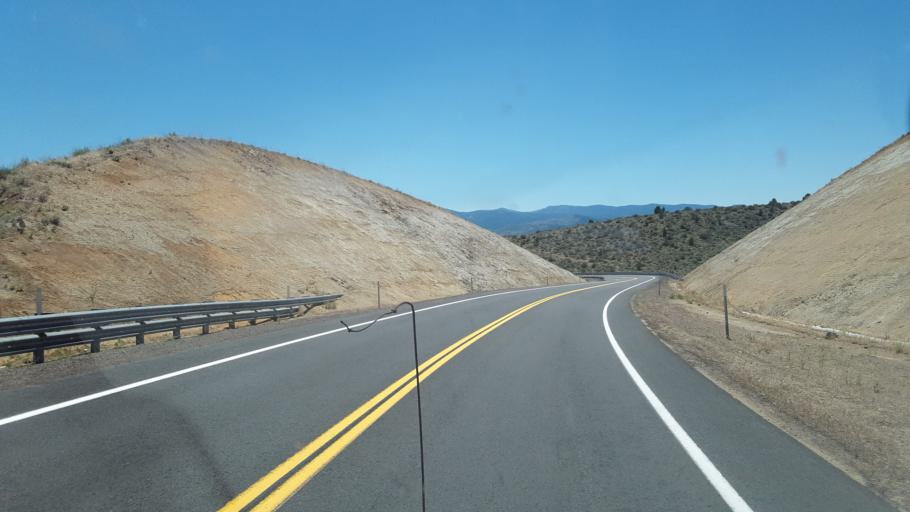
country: US
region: California
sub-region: Lassen County
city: Johnstonville
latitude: 40.4608
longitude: -120.5787
